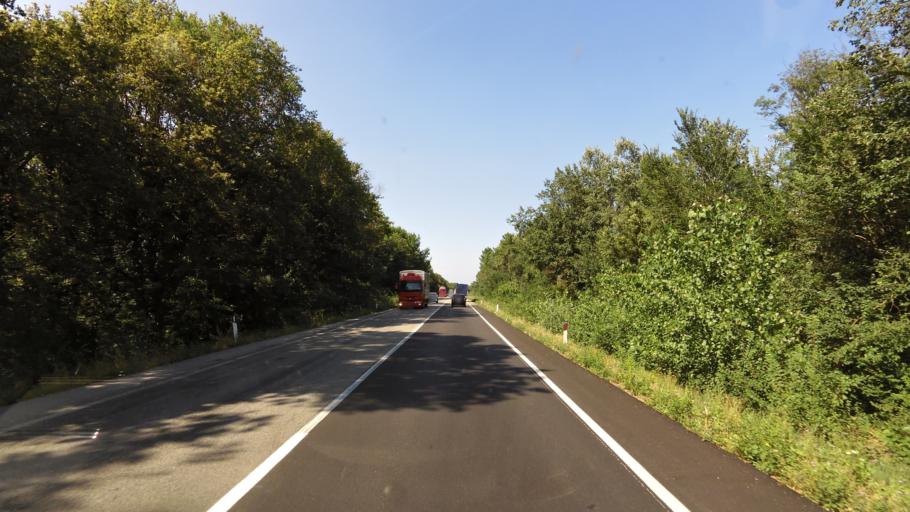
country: IT
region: Emilia-Romagna
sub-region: Provincia di Ravenna
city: Marina Romea
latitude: 44.4935
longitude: 12.2156
